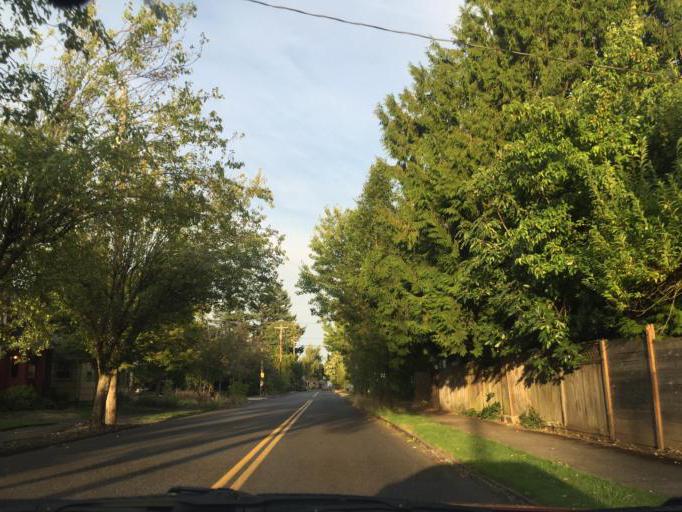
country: US
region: Oregon
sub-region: Multnomah County
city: Portland
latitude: 45.5551
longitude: -122.6285
